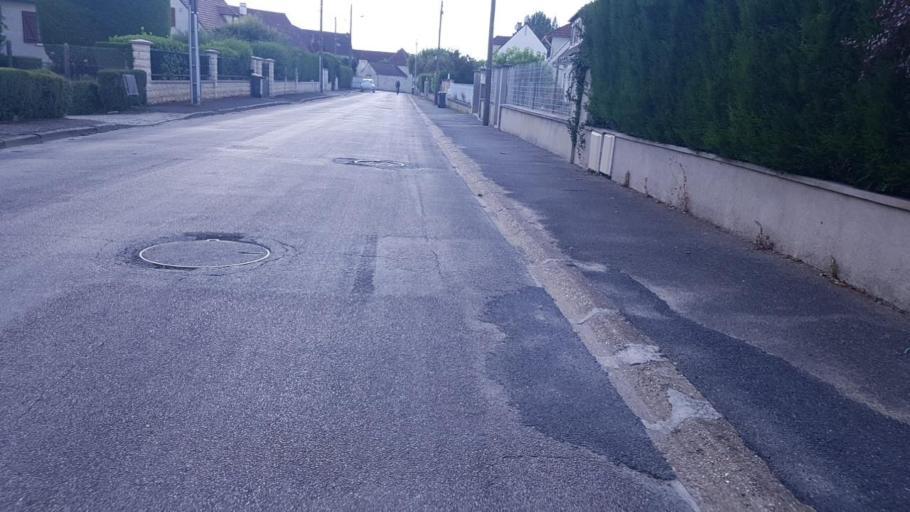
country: FR
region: Picardie
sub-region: Departement de l'Oise
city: Senlis
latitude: 49.1994
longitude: 2.5940
